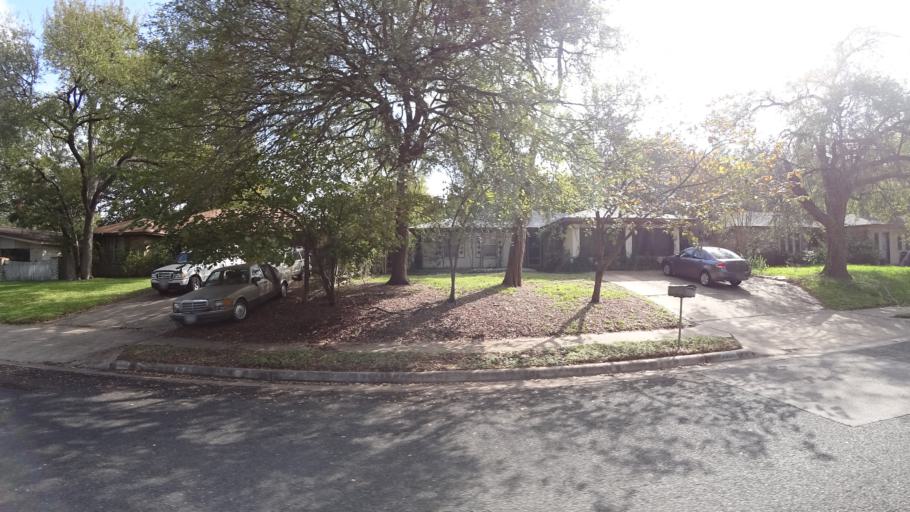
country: US
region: Texas
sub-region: Travis County
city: Shady Hollow
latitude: 30.2027
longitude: -97.8155
